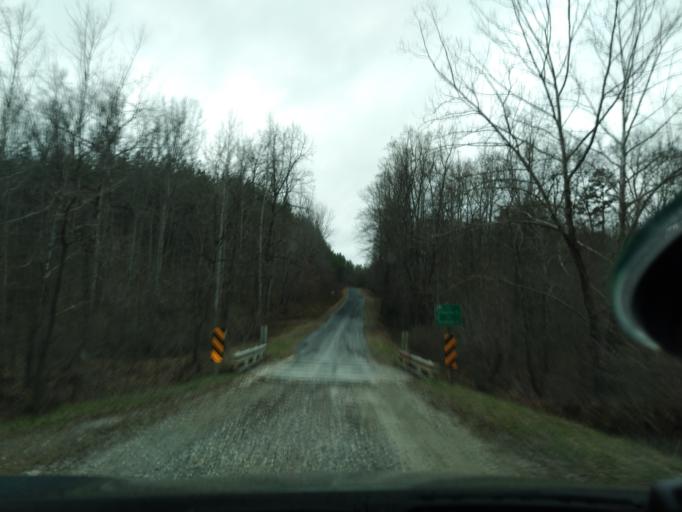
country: US
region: Virginia
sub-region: Buckingham County
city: Buckingham
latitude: 37.4237
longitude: -78.6595
